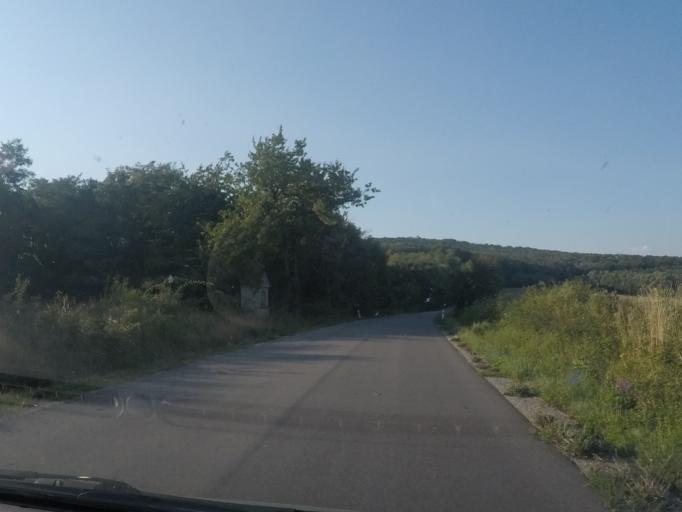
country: SK
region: Nitriansky
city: Zlate Moravce
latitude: 48.4377
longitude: 18.3203
